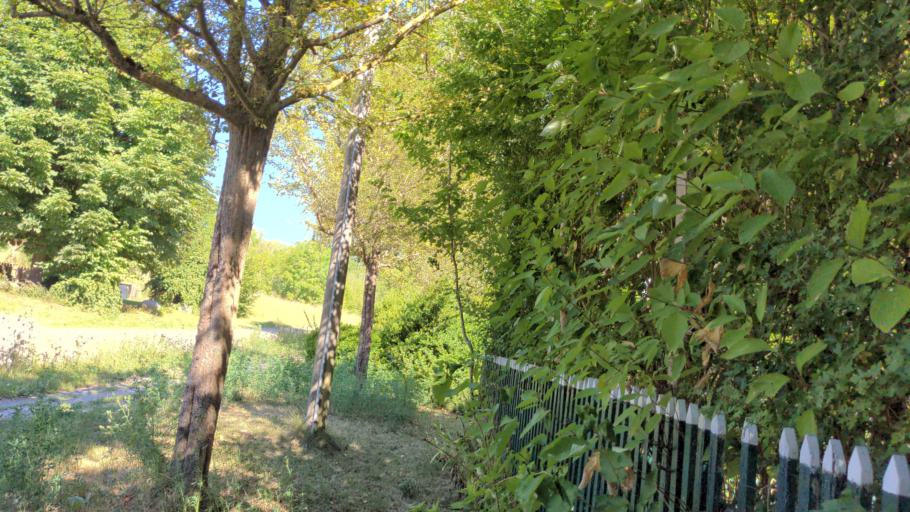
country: DE
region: Mecklenburg-Vorpommern
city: Selmsdorf
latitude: 53.8427
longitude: 10.8525
